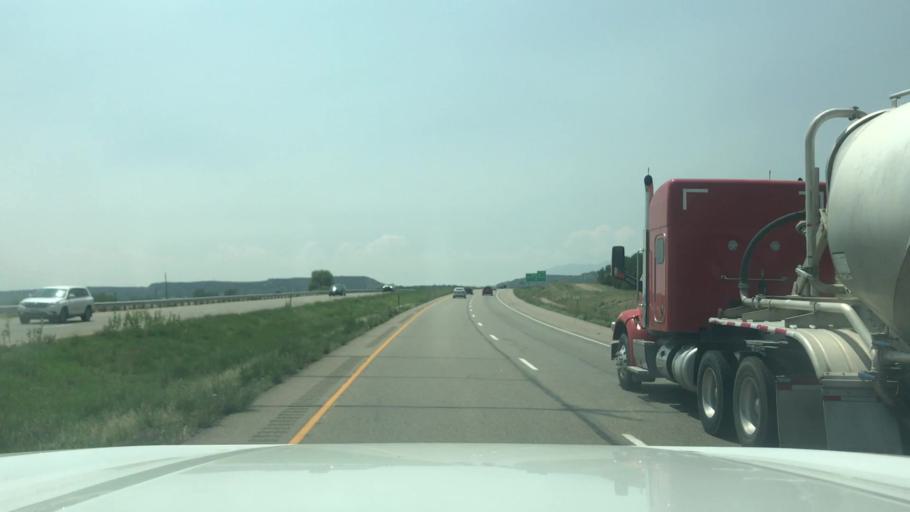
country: US
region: Colorado
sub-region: Pueblo County
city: Colorado City
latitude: 37.9997
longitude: -104.7567
